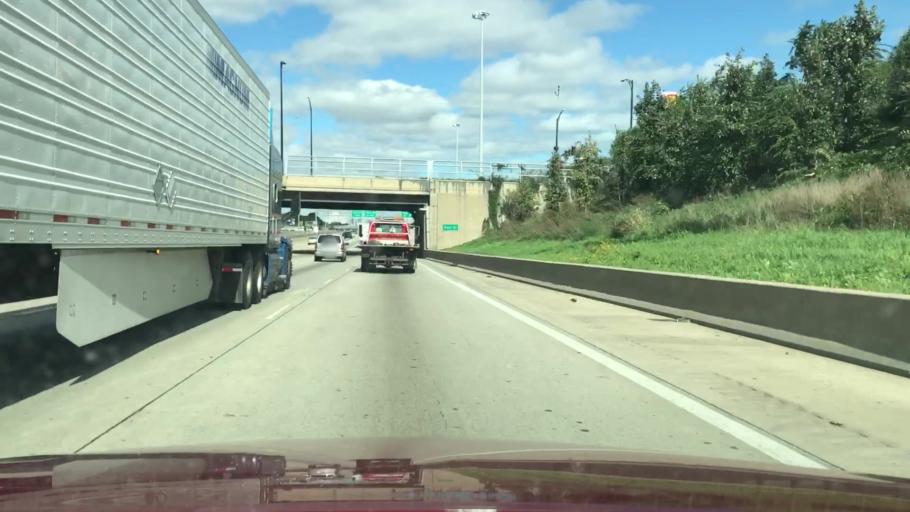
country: US
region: Illinois
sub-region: Cook County
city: Evergreen Park
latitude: 41.7429
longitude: -87.6247
